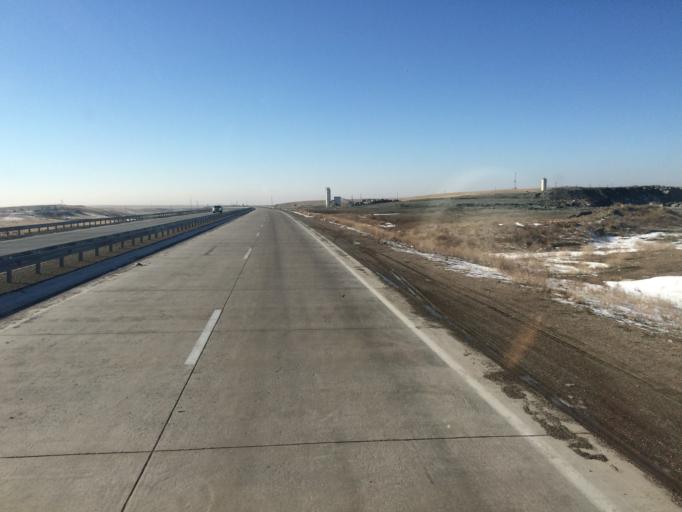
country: KZ
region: Zhambyl
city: Georgiyevka
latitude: 43.3555
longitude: 74.5743
